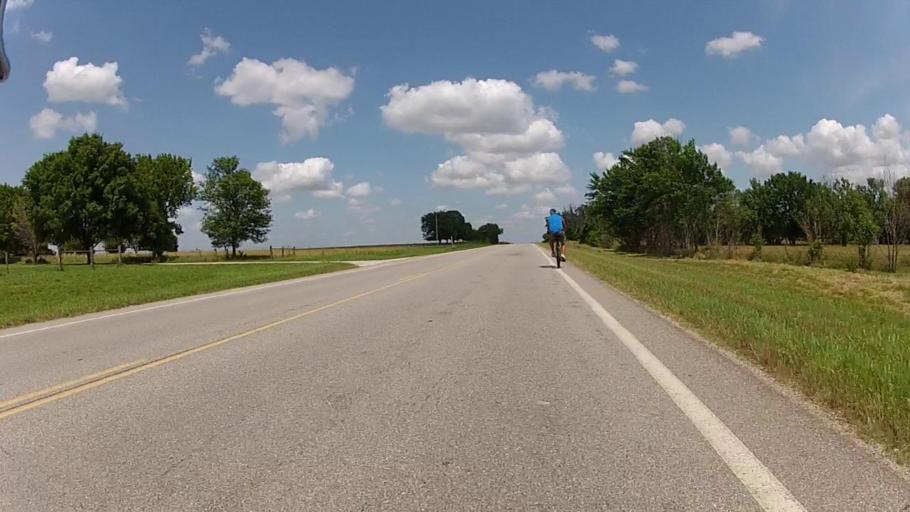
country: US
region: Kansas
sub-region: Labette County
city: Altamont
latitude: 37.1936
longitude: -95.2481
